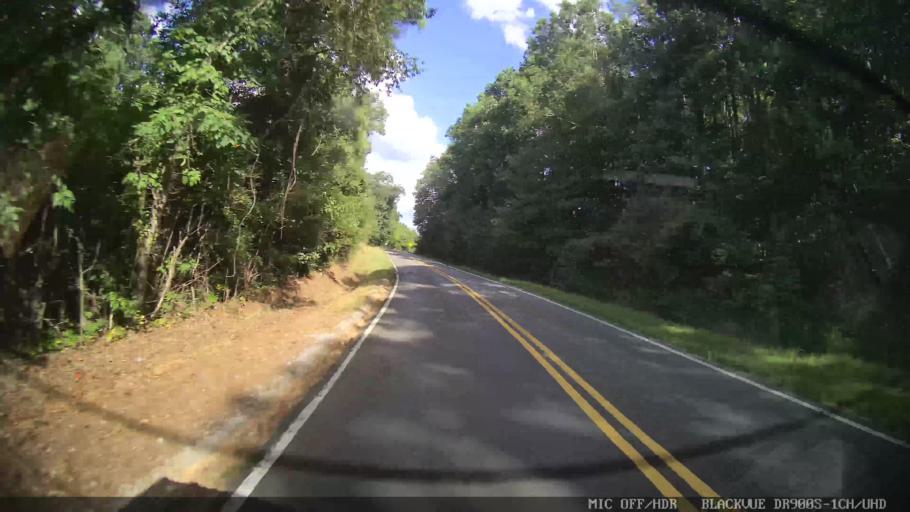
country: US
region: Georgia
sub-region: Floyd County
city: Lindale
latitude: 34.2030
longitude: -85.1164
